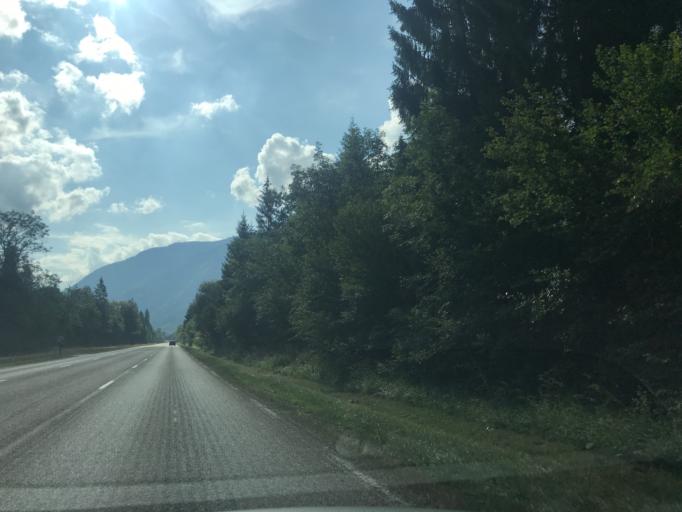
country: FR
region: Rhone-Alpes
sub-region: Departement de la Haute-Savoie
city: Dingy-Saint-Clair
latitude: 45.8974
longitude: 6.2225
